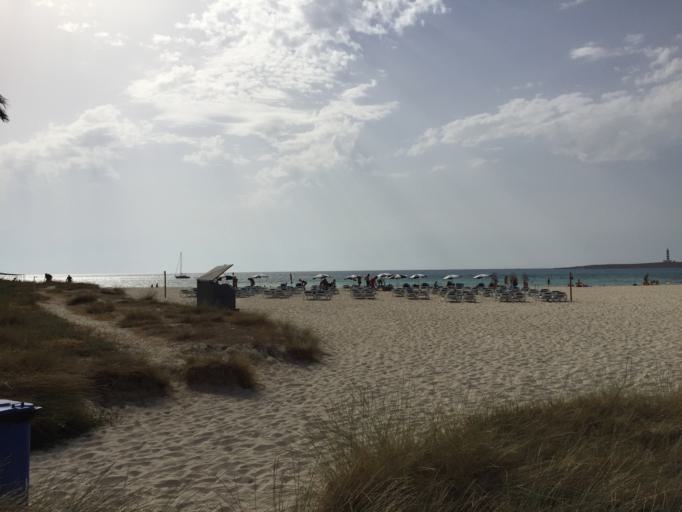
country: ES
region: Balearic Islands
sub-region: Illes Balears
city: Sant Lluis
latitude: 39.8140
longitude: 4.2799
